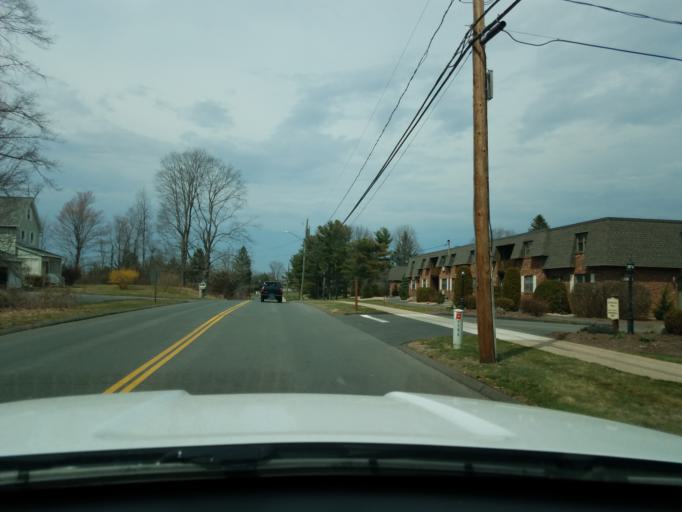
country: US
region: Connecticut
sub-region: Hartford County
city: Newington
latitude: 41.6604
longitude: -72.7167
